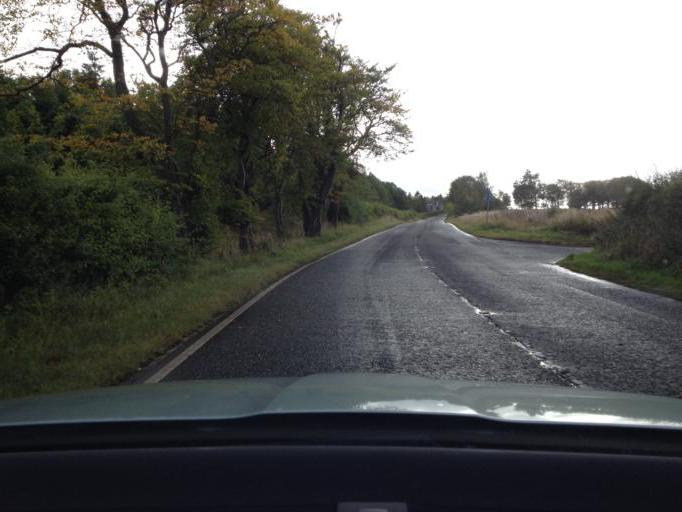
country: GB
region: Scotland
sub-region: West Lothian
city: West Calder
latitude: 55.8262
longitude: -3.5350
